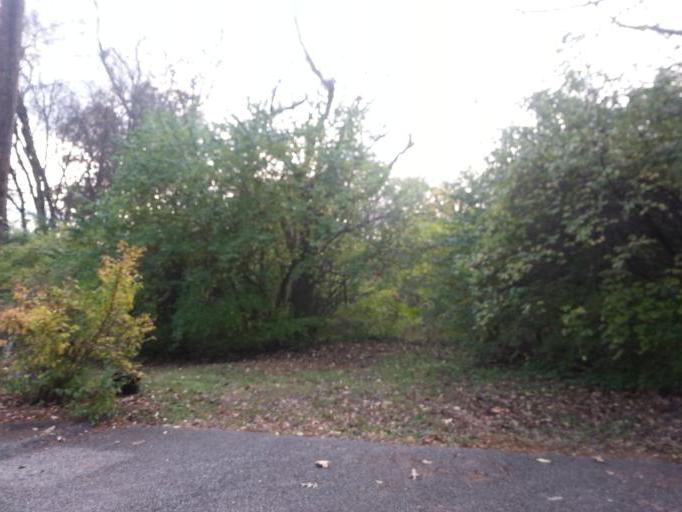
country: US
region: Tennessee
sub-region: Blount County
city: Louisville
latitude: 35.9132
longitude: -84.0463
